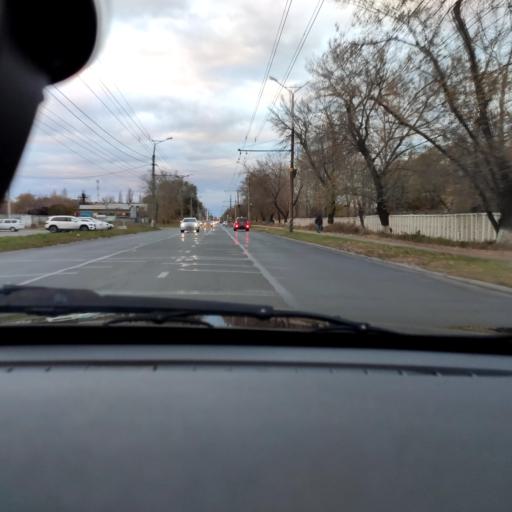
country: RU
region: Samara
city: Tol'yatti
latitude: 53.5257
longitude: 49.4353
